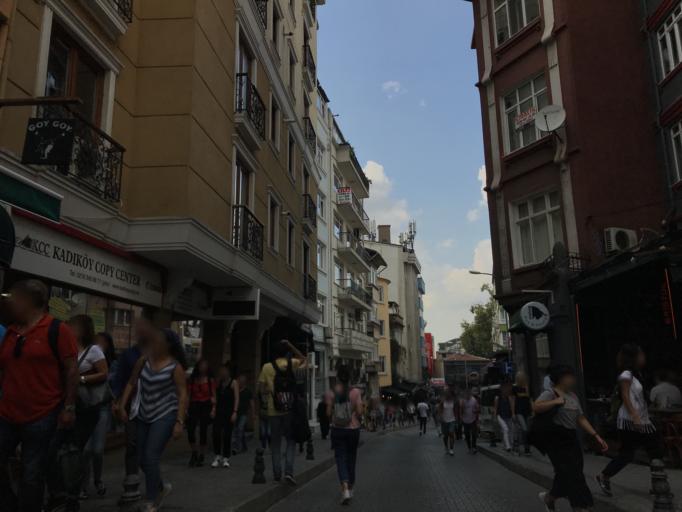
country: TR
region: Istanbul
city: UEskuedar
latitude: 40.9879
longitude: 29.0242
